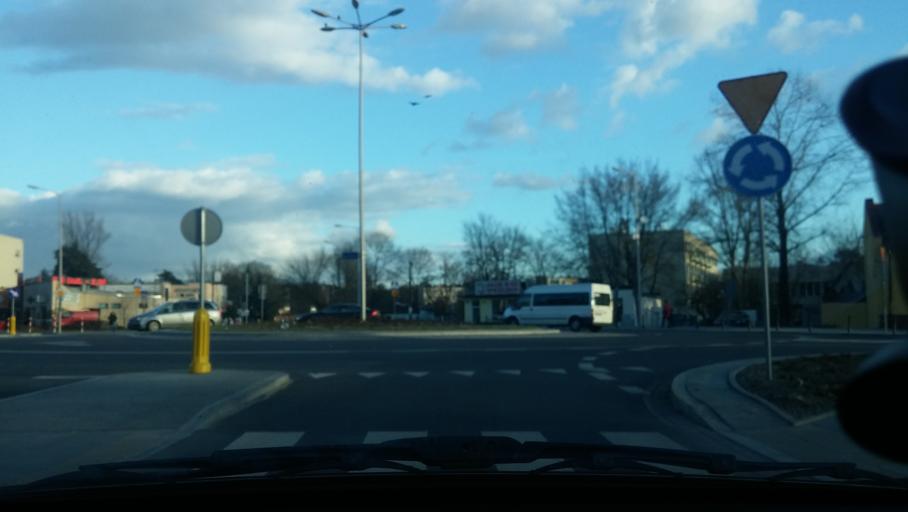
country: PL
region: Masovian Voivodeship
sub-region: Warszawa
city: Wawer
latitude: 52.2064
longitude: 21.1744
